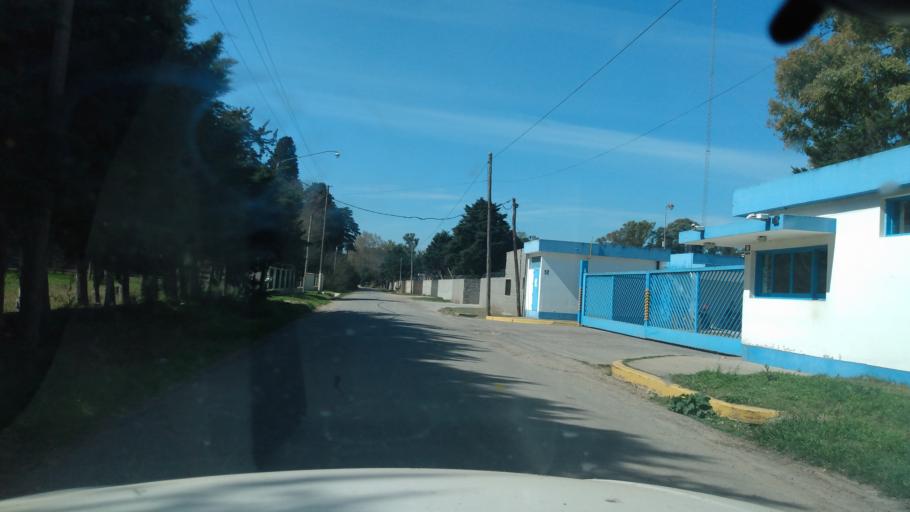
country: AR
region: Buenos Aires
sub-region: Partido de Lujan
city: Lujan
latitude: -34.5734
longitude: -59.1322
